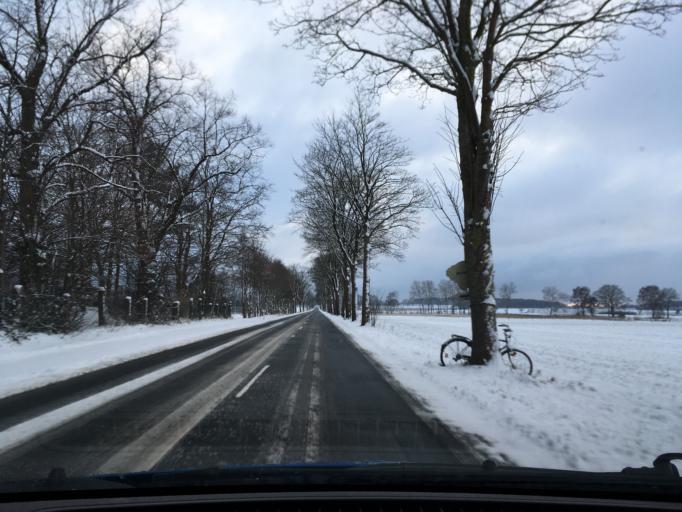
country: DE
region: Lower Saxony
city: Wulfsen
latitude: 53.3188
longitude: 10.1777
